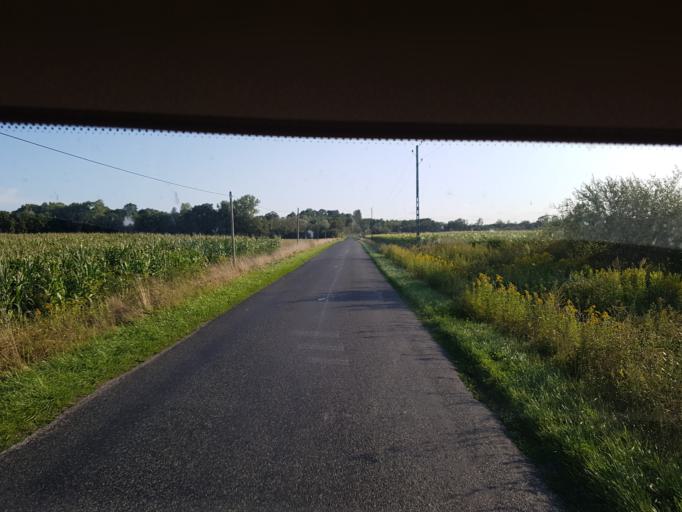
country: FR
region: Rhone-Alpes
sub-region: Departement de l'Ain
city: Villars-les-Dombes
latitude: 45.9733
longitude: 5.0882
